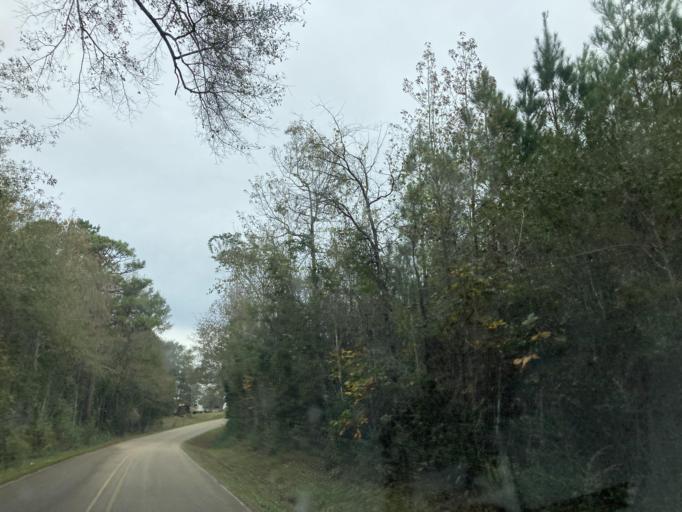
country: US
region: Mississippi
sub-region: Lamar County
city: Lumberton
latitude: 31.0373
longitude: -89.4547
